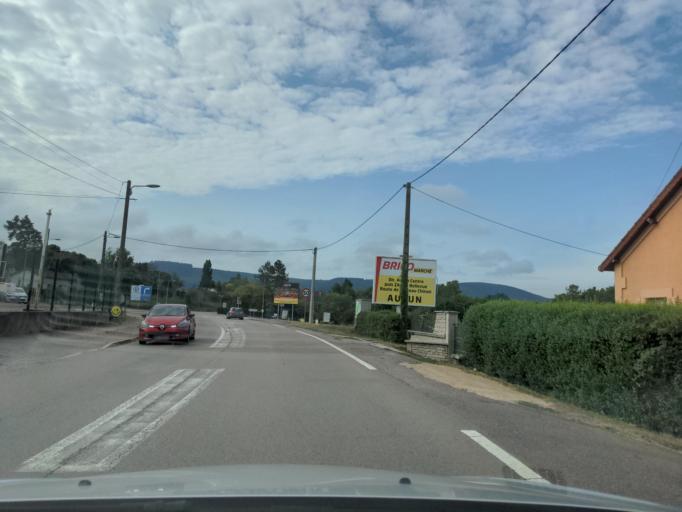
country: FR
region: Bourgogne
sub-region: Departement de Saone-et-Loire
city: Autun
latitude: 46.9685
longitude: 4.3053
